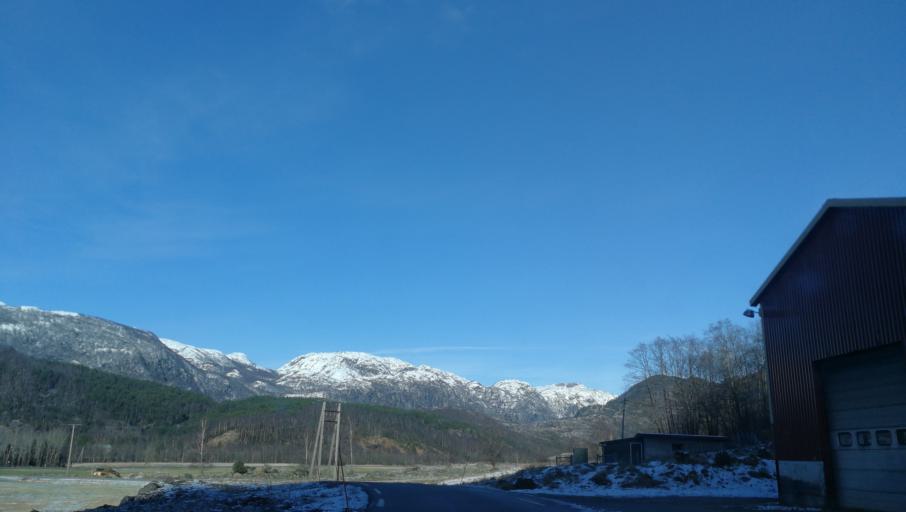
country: NO
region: Rogaland
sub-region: Hjelmeland
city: Hjelmelandsvagen
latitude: 59.1287
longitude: 6.2761
